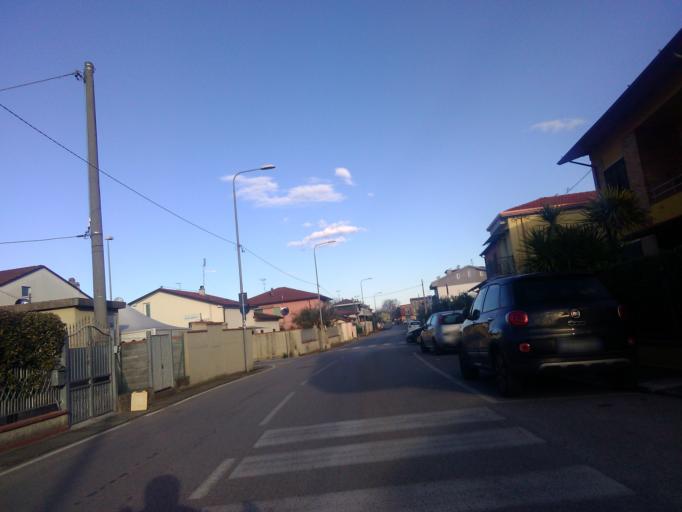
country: IT
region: Tuscany
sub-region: Provincia di Massa-Carrara
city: Carrara
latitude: 44.0571
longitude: 10.0482
